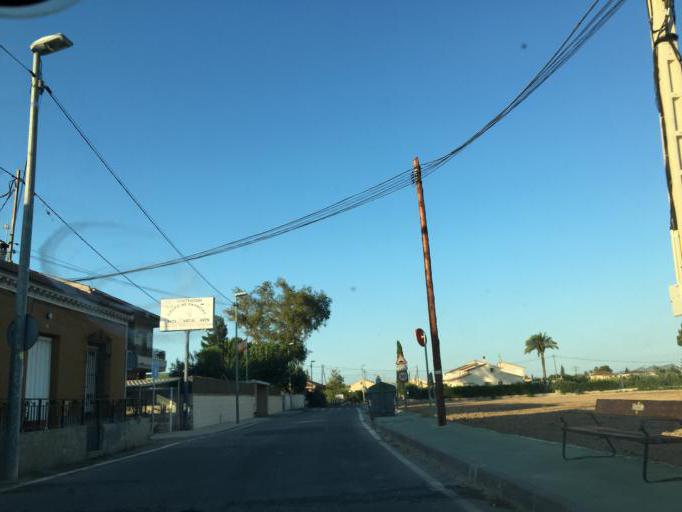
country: ES
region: Murcia
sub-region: Murcia
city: Santomera
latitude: 38.0132
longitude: -1.0622
